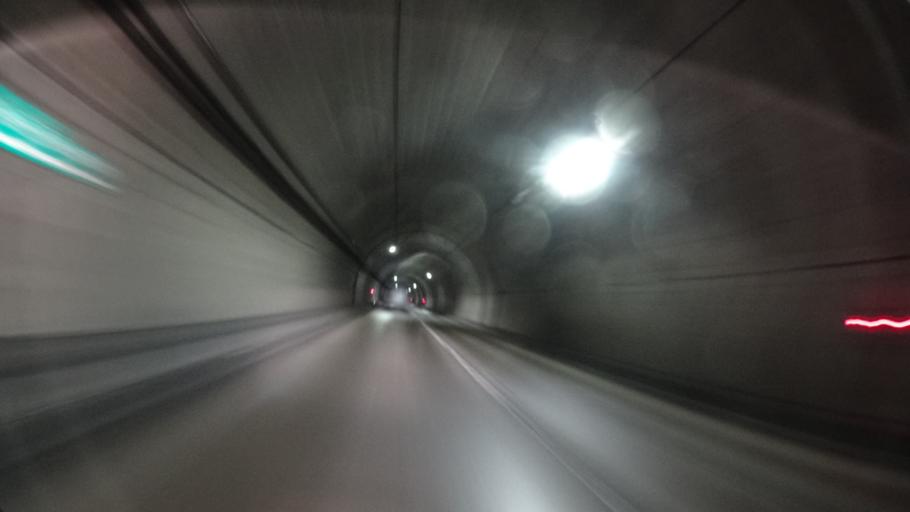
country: JP
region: Fukui
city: Maruoka
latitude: 36.1303
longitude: 136.3237
